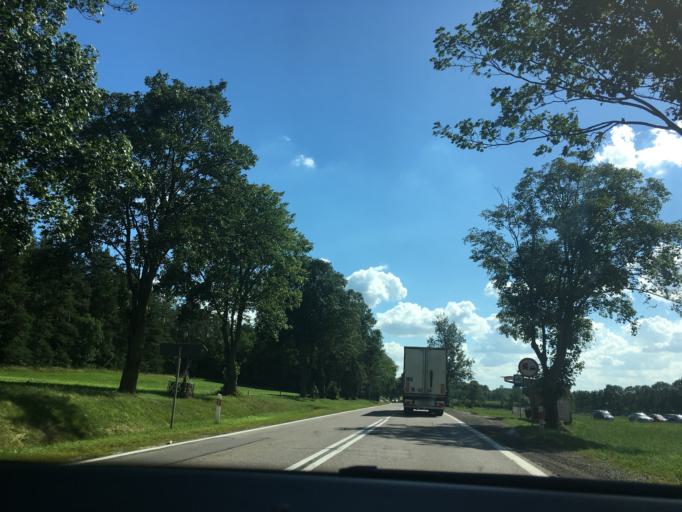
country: PL
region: Podlasie
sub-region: Powiat sokolski
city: Suchowola
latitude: 53.6131
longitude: 23.1202
